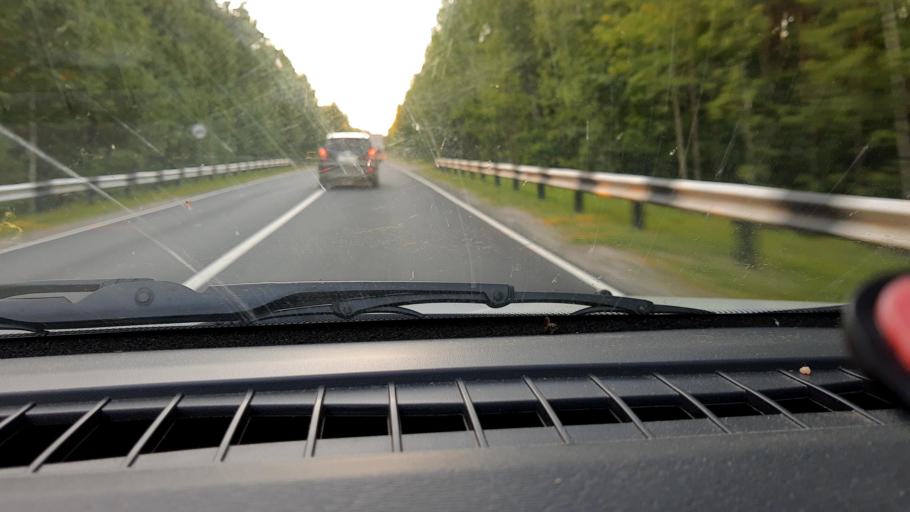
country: RU
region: Nizjnij Novgorod
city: Krasnyye Baki
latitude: 57.1234
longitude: 45.2109
